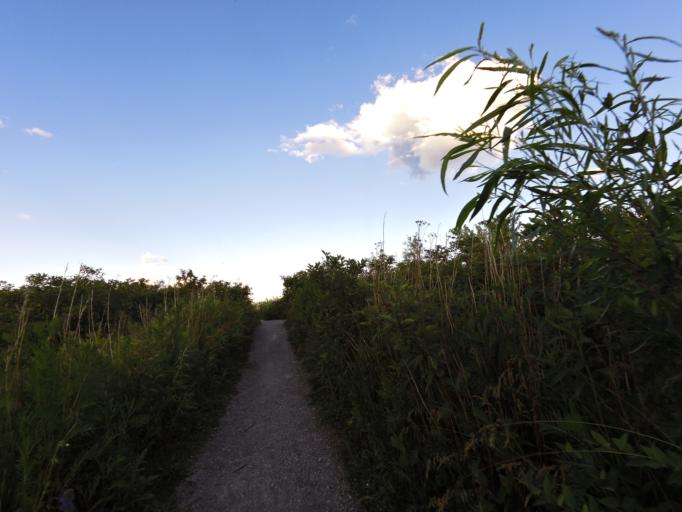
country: CA
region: Ontario
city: Toronto
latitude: 43.6267
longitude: -79.3313
